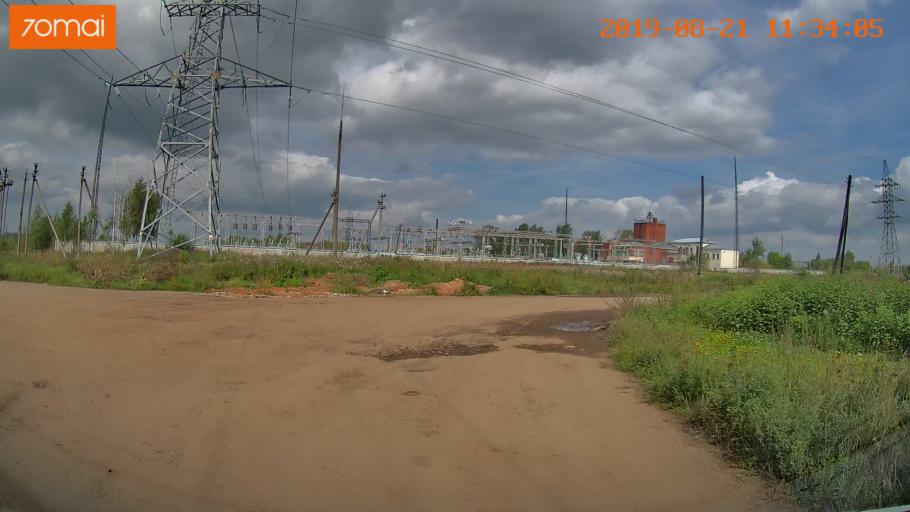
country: RU
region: Ivanovo
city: Novo-Talitsy
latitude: 56.9870
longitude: 40.9105
